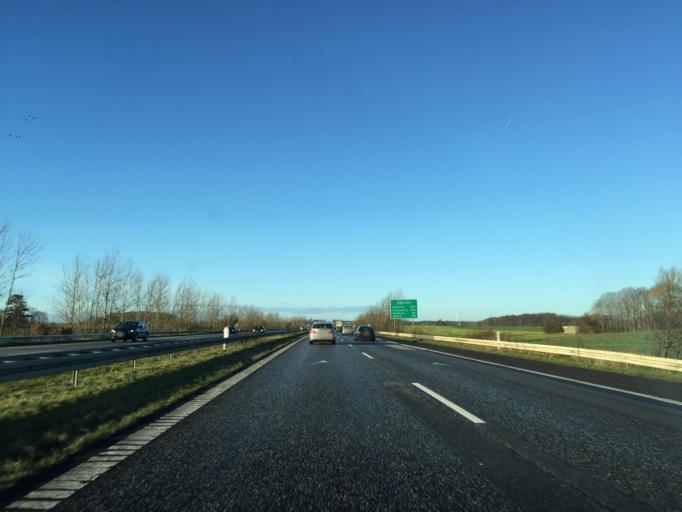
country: DK
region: South Denmark
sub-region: Middelfart Kommune
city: Ejby
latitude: 55.4319
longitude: 9.9874
